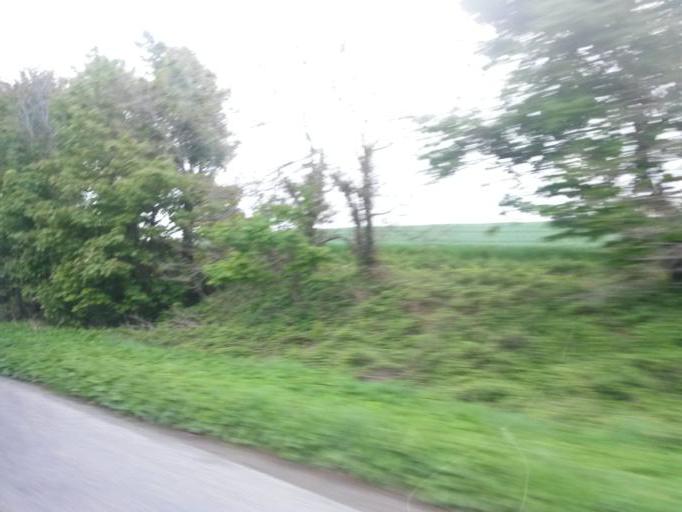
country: IE
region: Leinster
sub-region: Loch Garman
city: Enniscorthy
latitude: 52.4825
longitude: -6.5646
